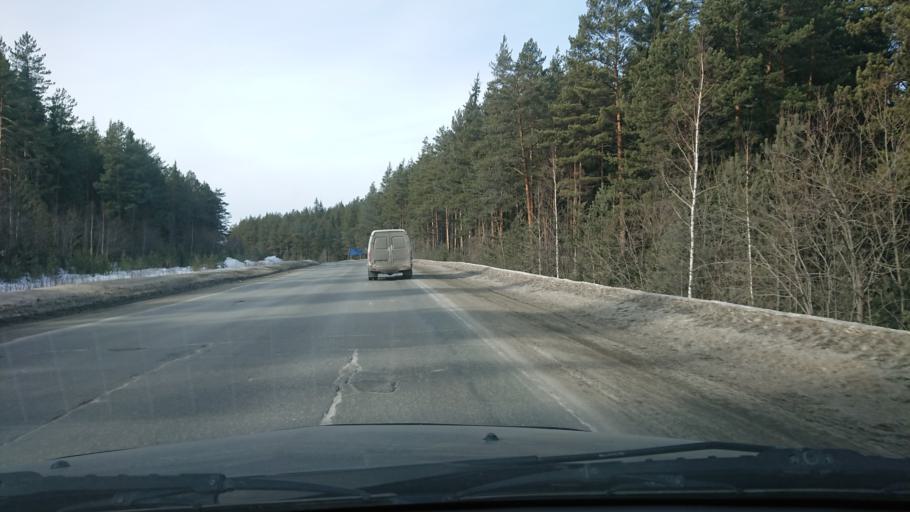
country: RU
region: Sverdlovsk
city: Revda
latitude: 56.7973
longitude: 59.9945
